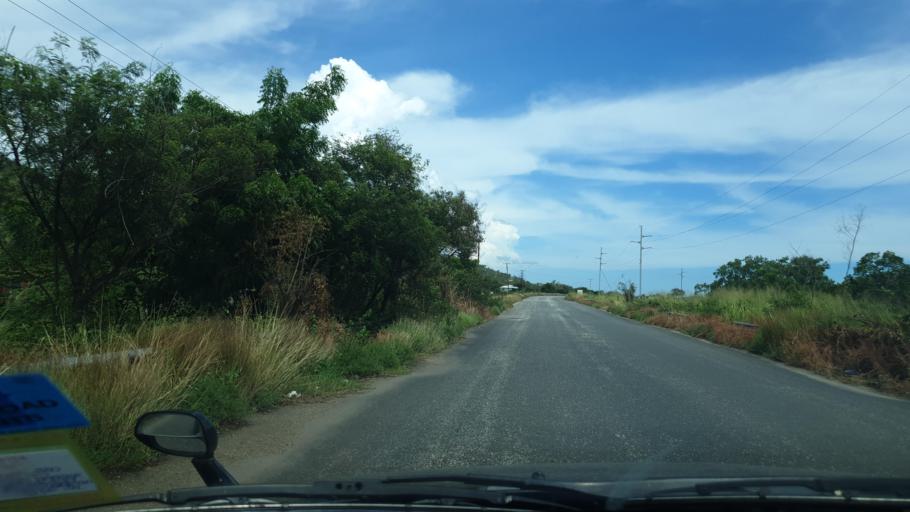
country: PG
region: National Capital
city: Port Moresby
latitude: -9.4081
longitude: 147.0696
